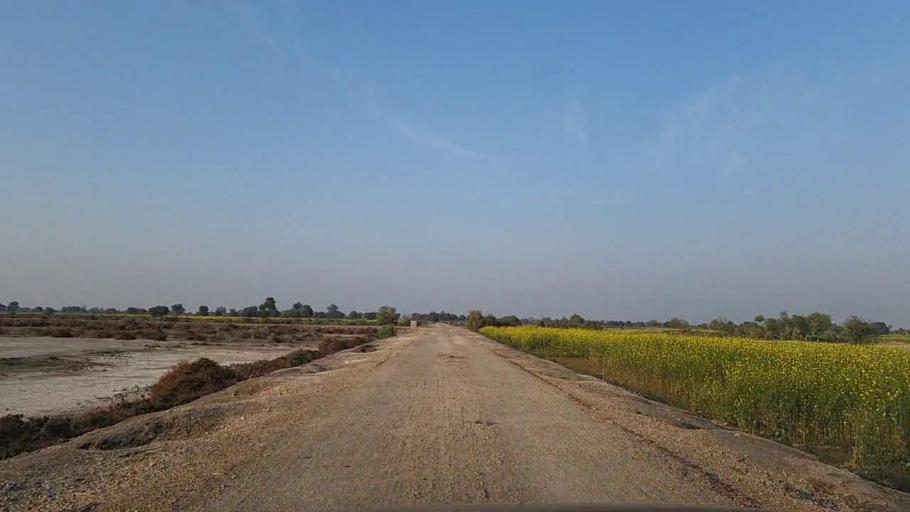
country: PK
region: Sindh
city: Jam Sahib
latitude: 26.3825
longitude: 68.5390
